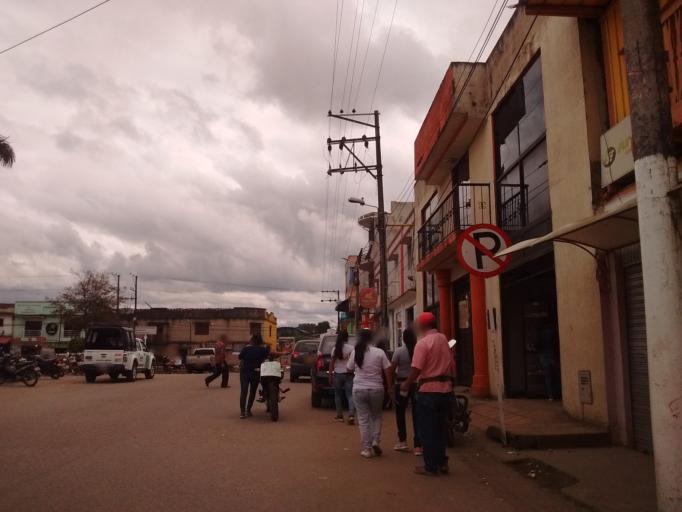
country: CO
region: Huila
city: Isnos
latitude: 1.9299
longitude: -76.2146
